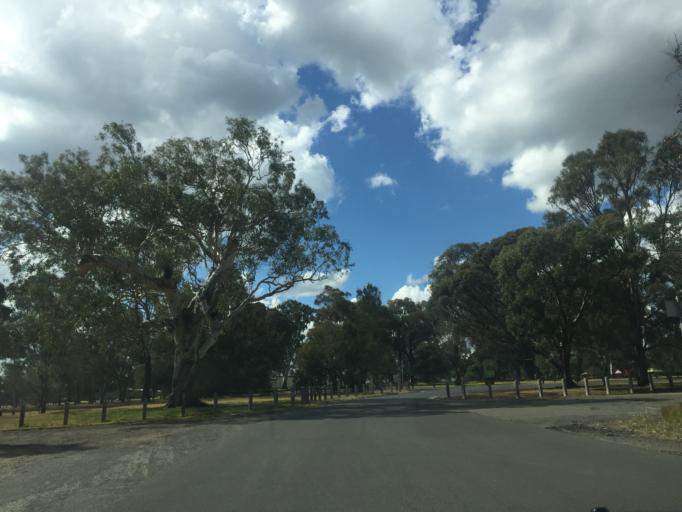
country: AU
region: Victoria
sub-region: Darebin
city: Kingsbury
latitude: -37.7122
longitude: 145.0437
